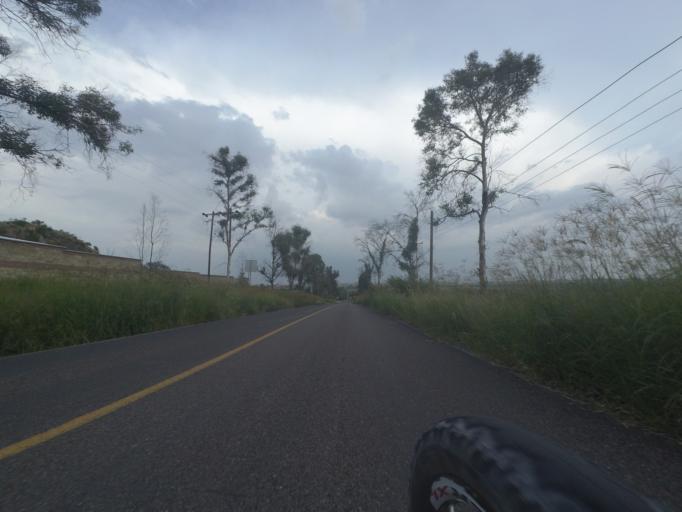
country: MX
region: Aguascalientes
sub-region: Aguascalientes
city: La Loma de los Negritos
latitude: 21.8373
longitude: -102.3743
